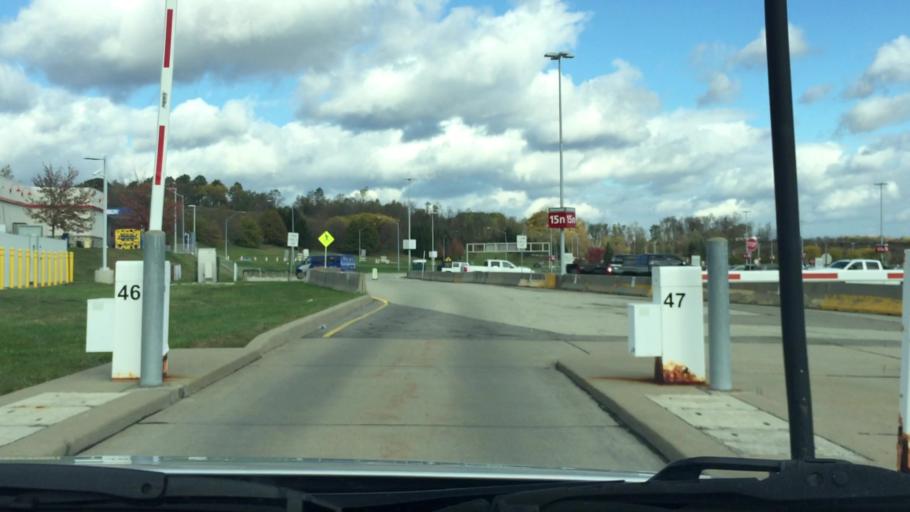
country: US
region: Pennsylvania
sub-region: Allegheny County
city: Imperial
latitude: 40.4937
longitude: -80.2666
